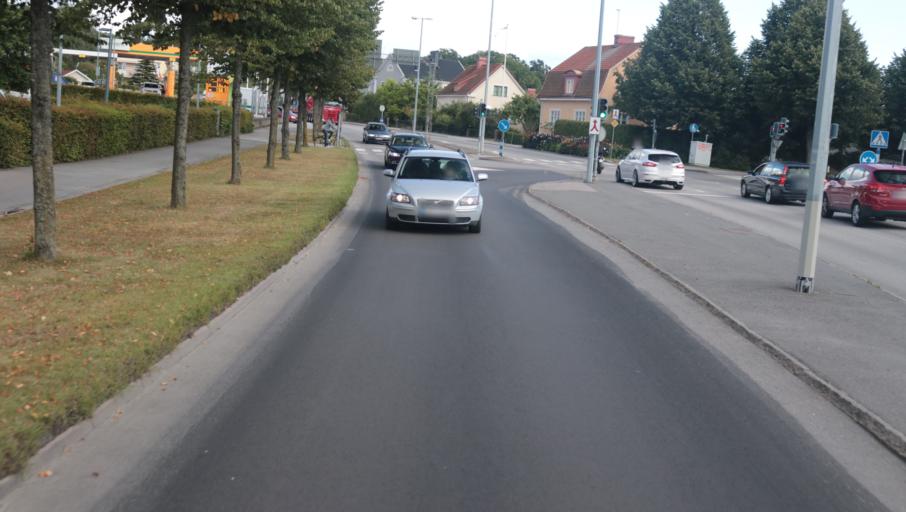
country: SE
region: Blekinge
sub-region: Karlshamns Kommun
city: Karlshamn
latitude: 56.1777
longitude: 14.8564
